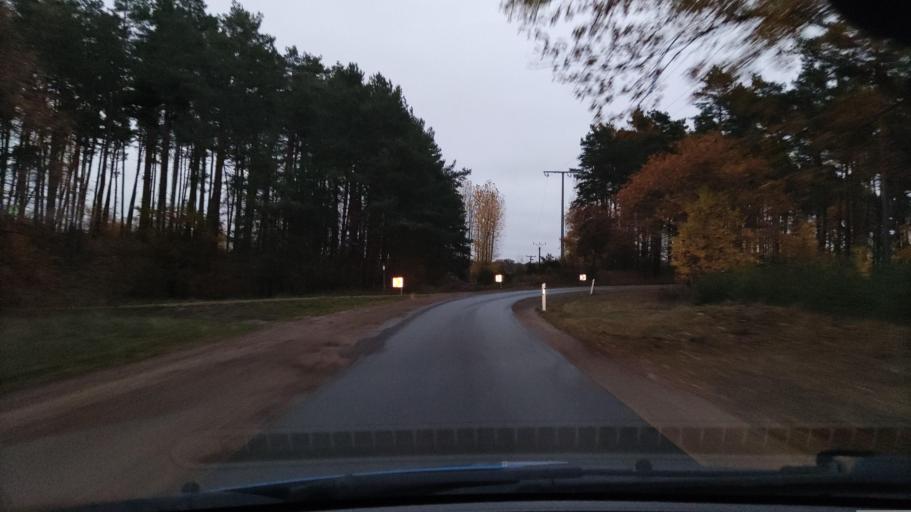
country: DE
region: Mecklenburg-Vorpommern
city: Neu Kaliss
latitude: 53.1838
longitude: 11.2551
